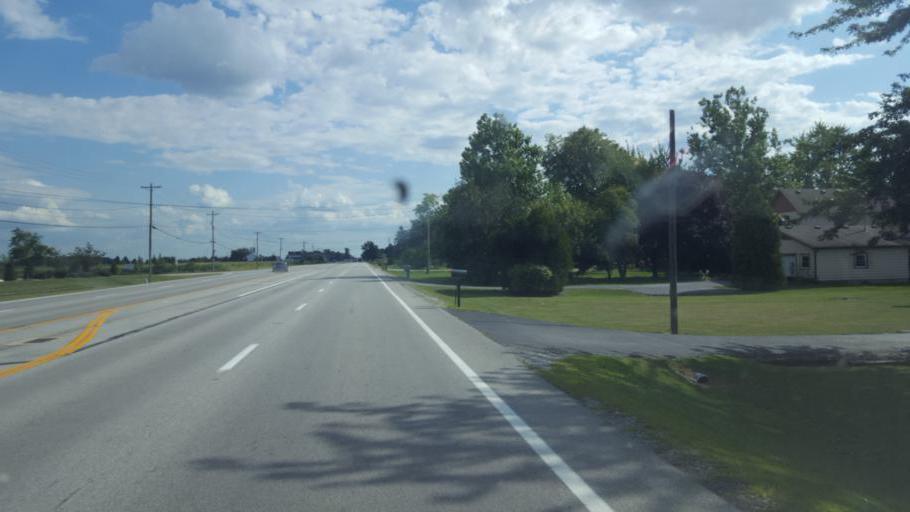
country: US
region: Ohio
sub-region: Wood County
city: Haskins
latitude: 41.4541
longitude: -83.6511
